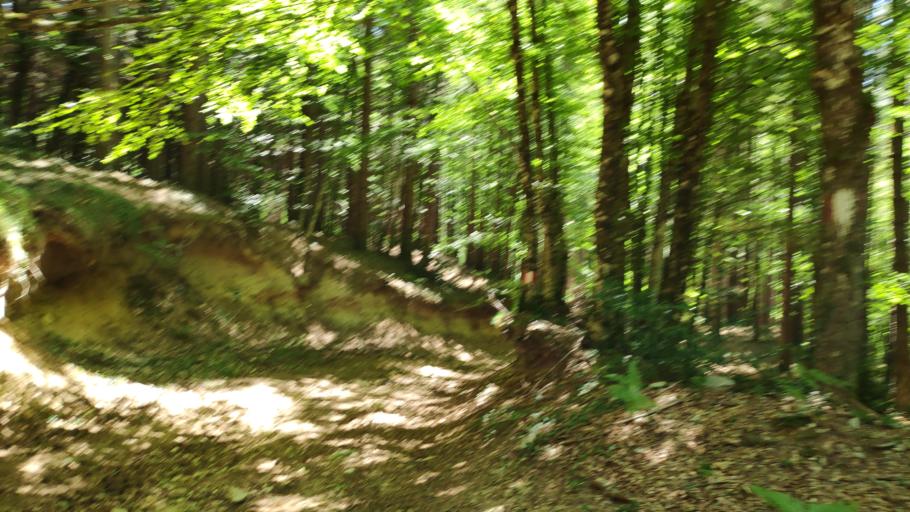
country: IT
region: Calabria
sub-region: Provincia di Vibo-Valentia
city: Nardodipace
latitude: 38.5052
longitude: 16.3738
